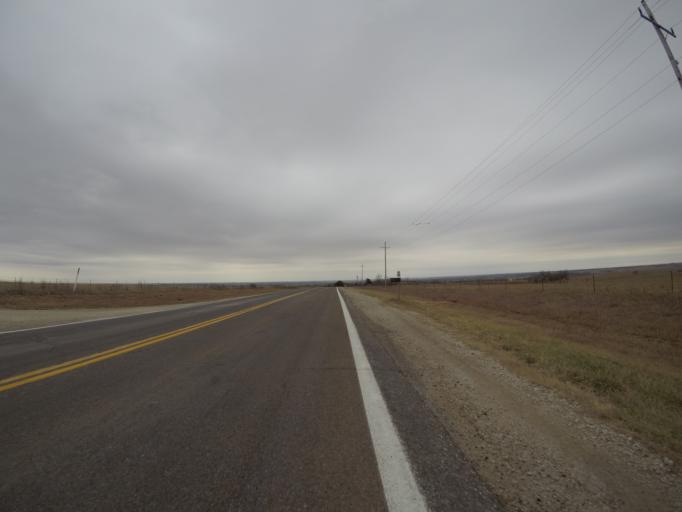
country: US
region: Kansas
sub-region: Wabaunsee County
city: Alma
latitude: 38.8638
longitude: -96.1190
